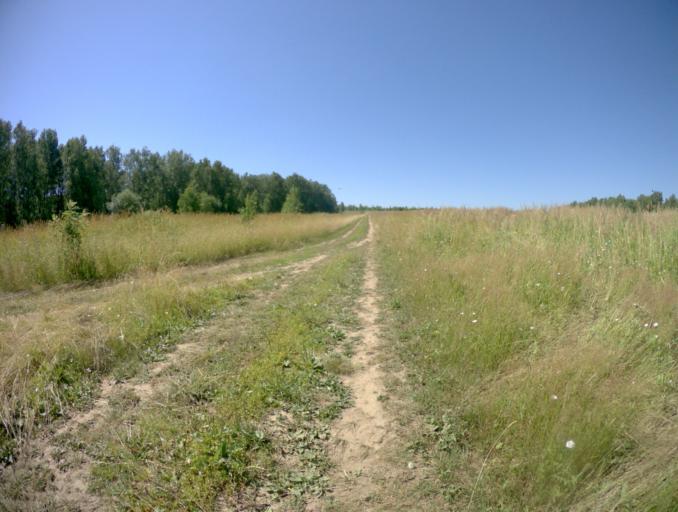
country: RU
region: Nizjnij Novgorod
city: Reshetikha
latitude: 56.1266
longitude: 43.2658
